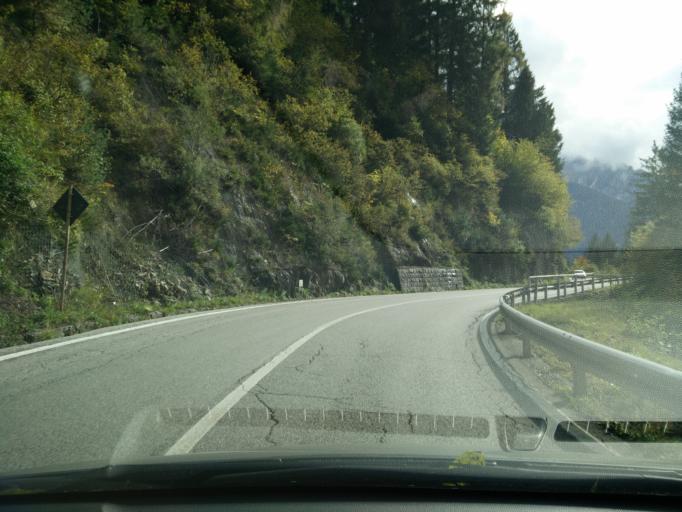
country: IT
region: Veneto
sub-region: Provincia di Belluno
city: Lozzo di Cadore
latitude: 46.4930
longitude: 12.4527
